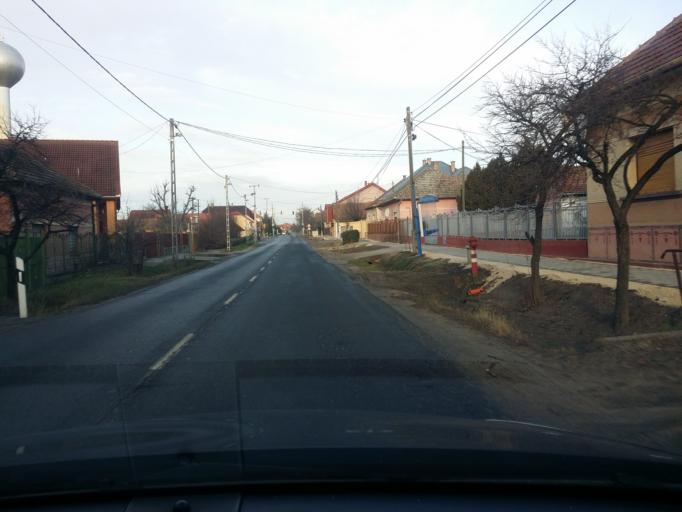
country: HU
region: Pest
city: Alsonemedi
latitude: 47.3178
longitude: 19.1555
